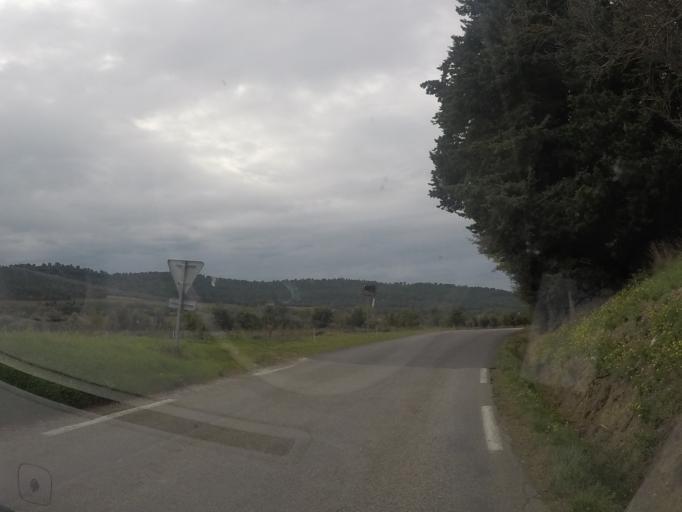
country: FR
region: Provence-Alpes-Cote d'Azur
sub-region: Departement du Vaucluse
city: Ansouis
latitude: 43.7425
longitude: 5.4378
